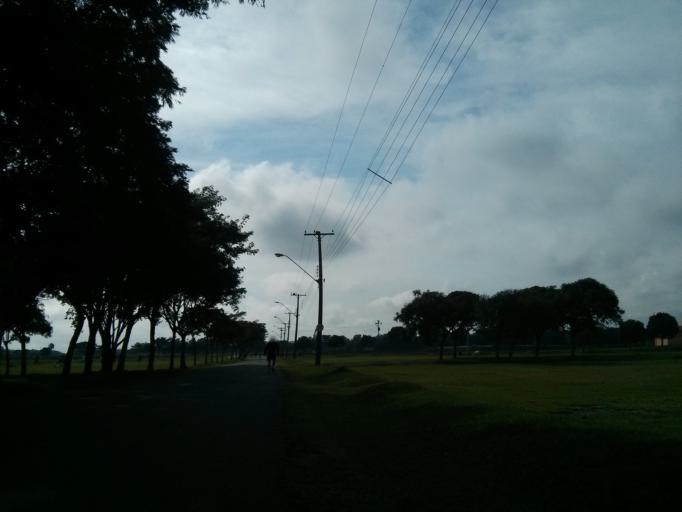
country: BR
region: Parana
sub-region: Sao Jose Dos Pinhais
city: Sao Jose dos Pinhais
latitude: -25.5189
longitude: -49.2214
